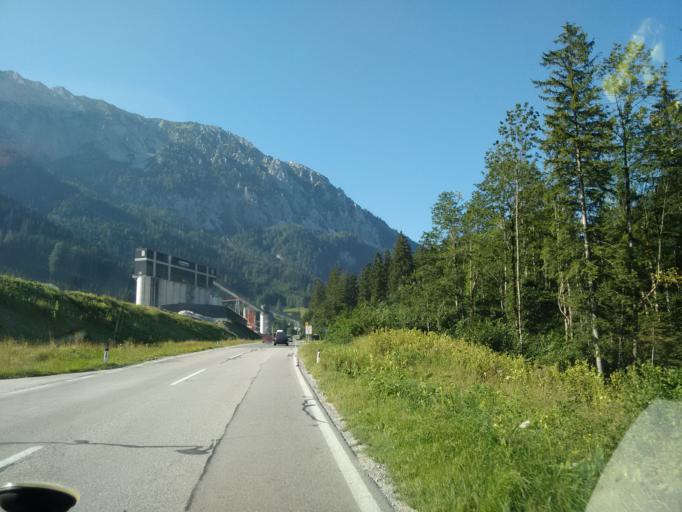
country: AT
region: Styria
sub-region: Politischer Bezirk Liezen
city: Ardning
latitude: 47.6425
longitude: 14.3320
